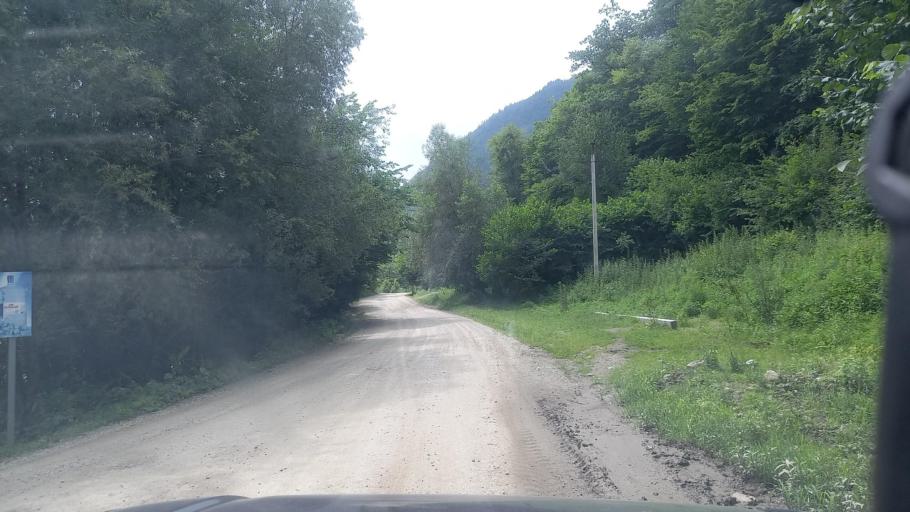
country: RU
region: Karachayevo-Cherkesiya
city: Kurdzhinovo
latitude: 43.9018
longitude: 40.9479
